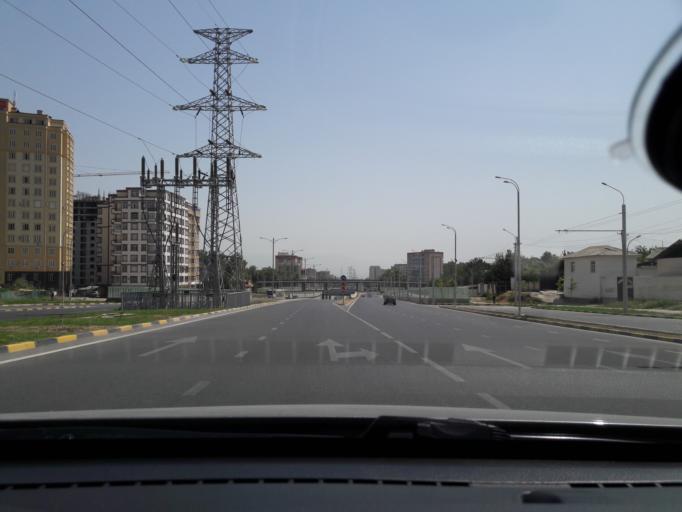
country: TJ
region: Dushanbe
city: Dushanbe
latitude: 38.5868
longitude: 68.7410
